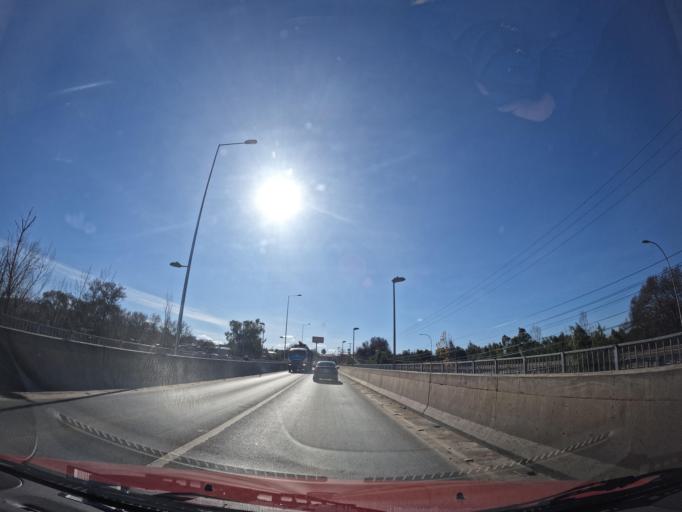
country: CL
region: Maule
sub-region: Provincia de Cauquenes
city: Cauquenes
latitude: -35.9743
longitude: -72.3152
